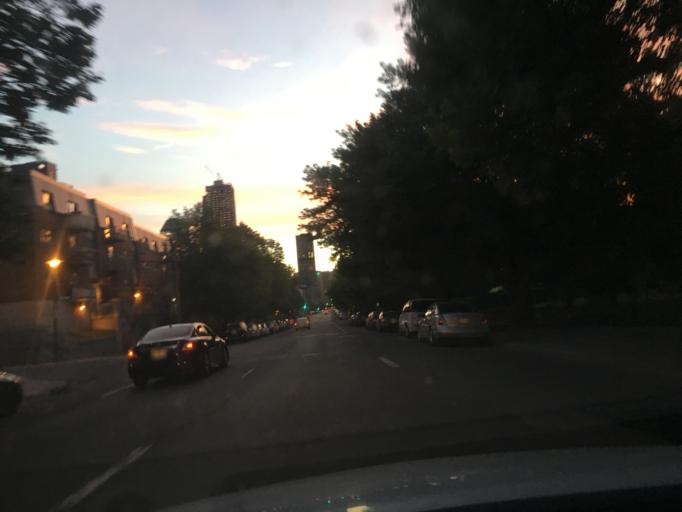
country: CA
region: Quebec
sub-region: Montreal
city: Montreal
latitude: 45.4895
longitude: -73.5718
